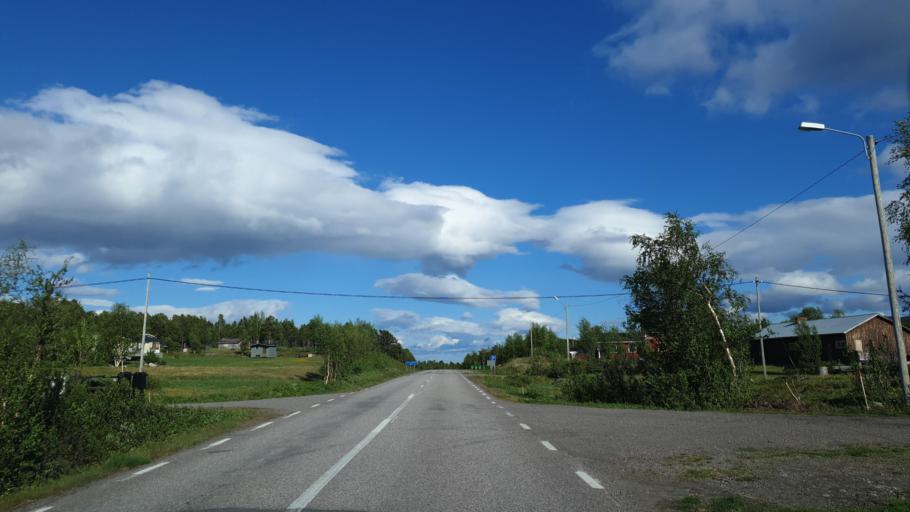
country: SE
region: Norrbotten
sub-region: Kiruna Kommun
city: Kiruna
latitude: 67.8735
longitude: 19.2189
